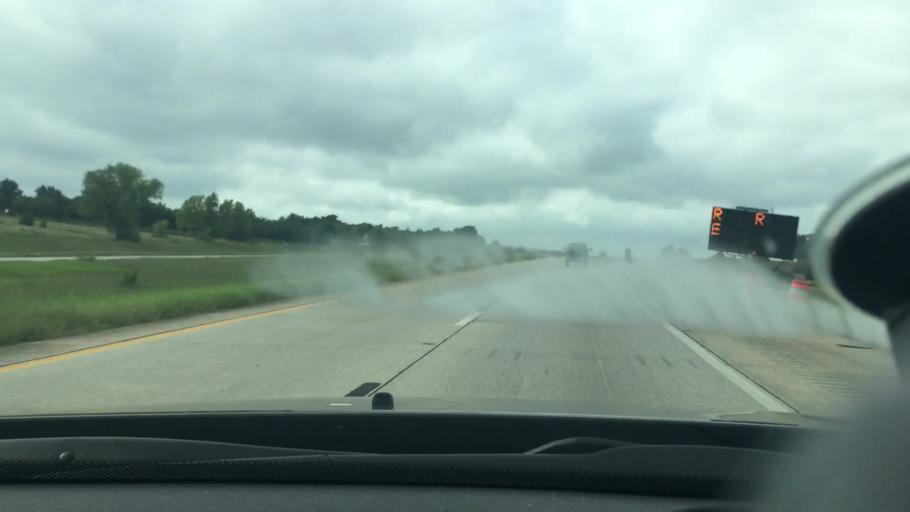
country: US
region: Oklahoma
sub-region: Bryan County
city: Durant
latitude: 34.1410
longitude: -96.2678
